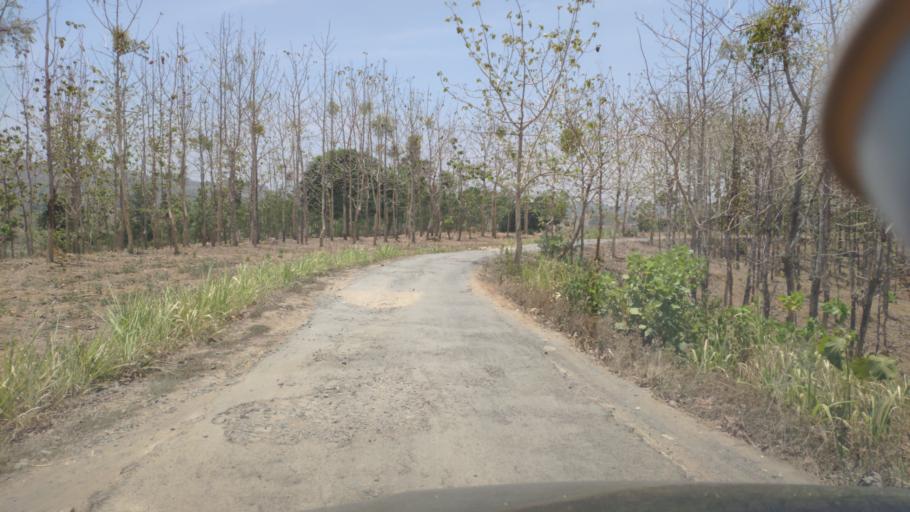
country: ID
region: Central Java
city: Padas
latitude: -6.9248
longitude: 111.1628
